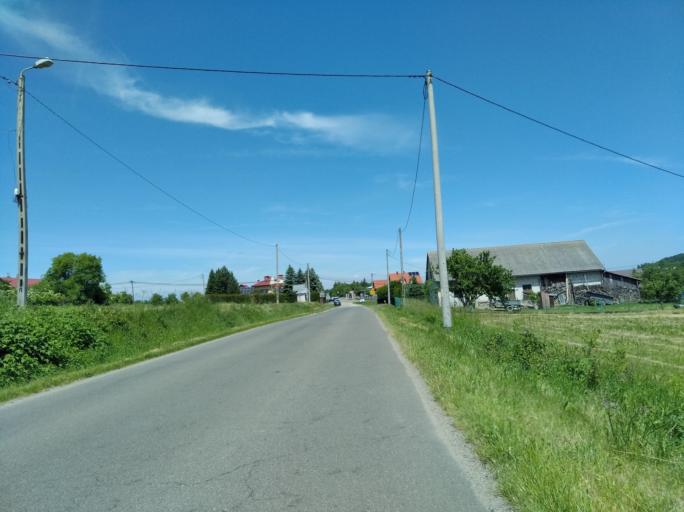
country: PL
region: Subcarpathian Voivodeship
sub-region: Powiat jasielski
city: Osiek Jasielski
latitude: 49.6707
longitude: 21.5435
